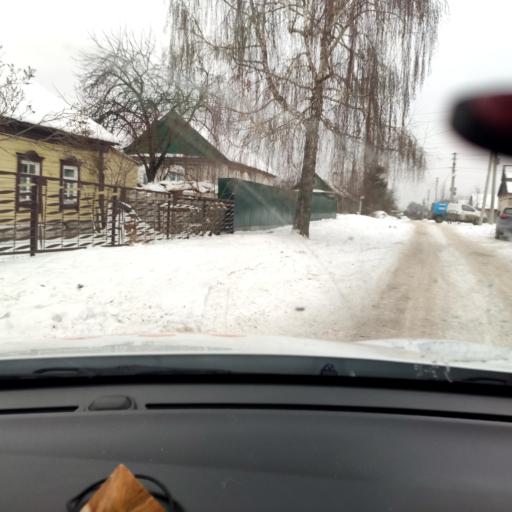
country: RU
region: Tatarstan
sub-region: Gorod Kazan'
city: Kazan
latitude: 55.8608
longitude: 49.0662
